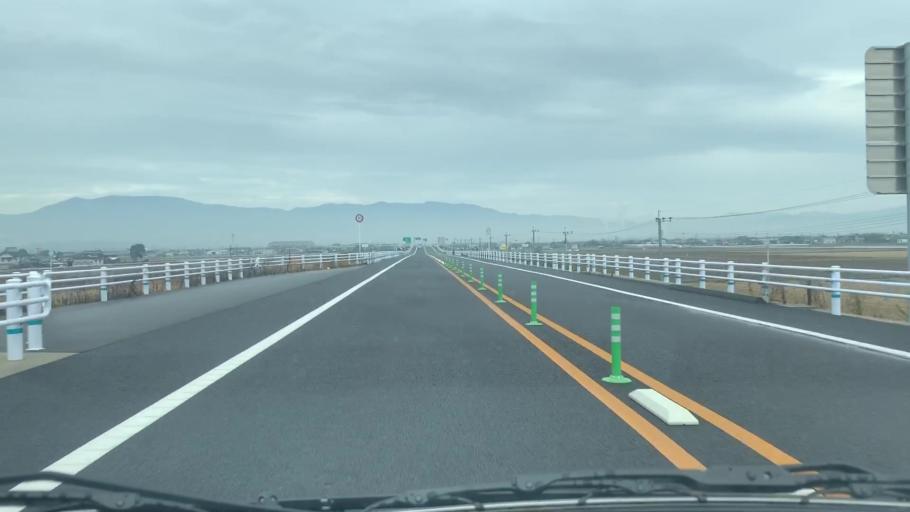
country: JP
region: Saga Prefecture
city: Saga-shi
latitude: 33.2107
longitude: 130.2148
